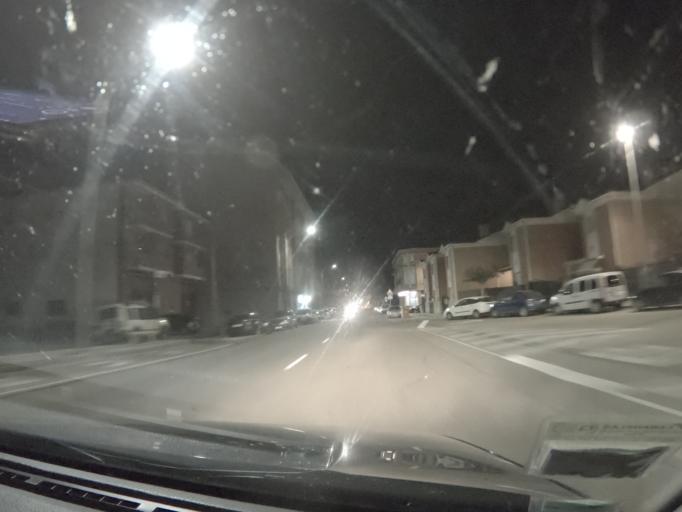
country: ES
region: Castille and Leon
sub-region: Provincia de Zamora
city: Benavente
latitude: 42.0070
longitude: -5.6712
